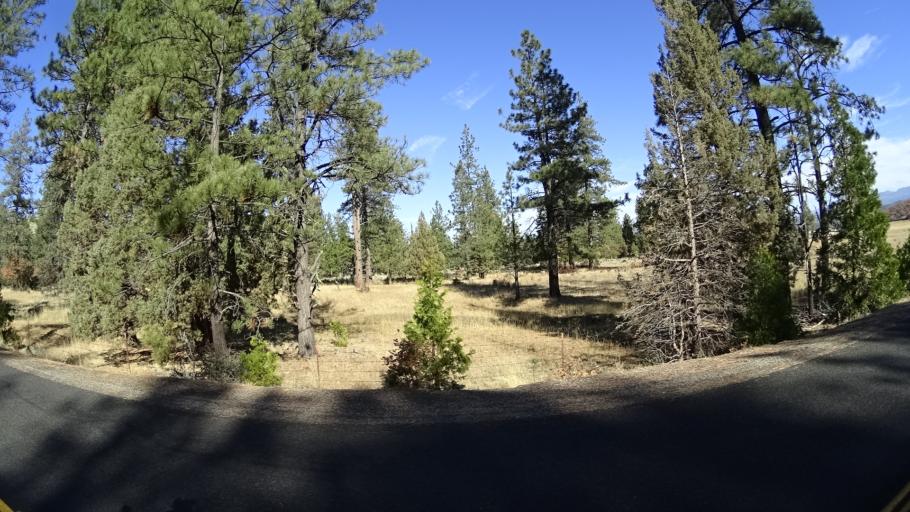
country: US
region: California
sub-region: Siskiyou County
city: Weed
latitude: 41.4363
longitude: -122.4634
